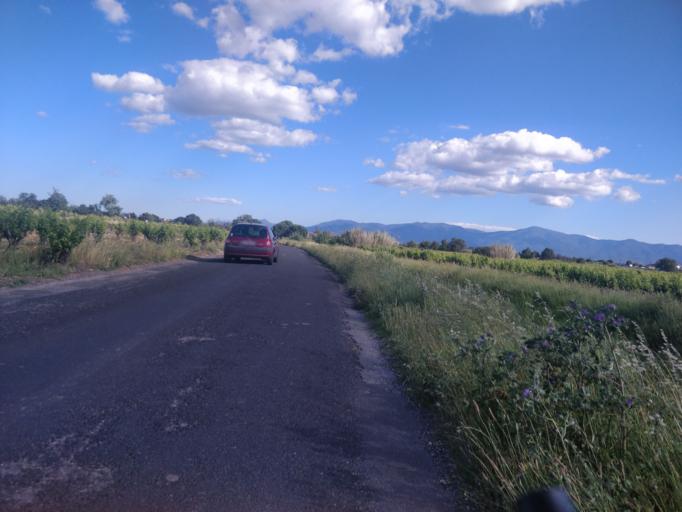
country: FR
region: Languedoc-Roussillon
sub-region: Departement des Pyrenees-Orientales
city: Cabestany
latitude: 42.6678
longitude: 2.9325
